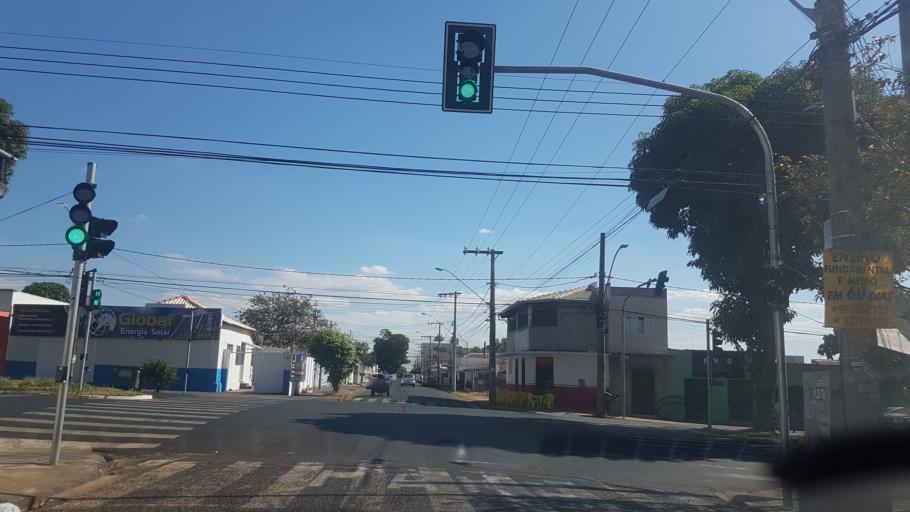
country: BR
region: Minas Gerais
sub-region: Uberlandia
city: Uberlandia
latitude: -18.9085
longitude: -48.2878
